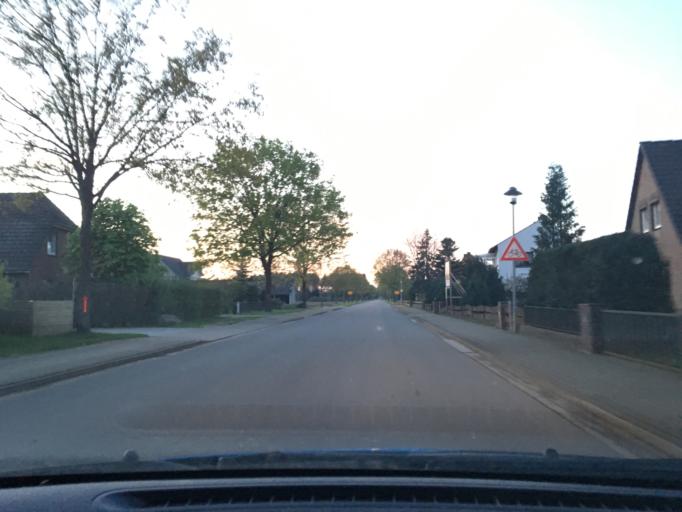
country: DE
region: Lower Saxony
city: Oldendorf
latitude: 53.1603
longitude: 10.2131
